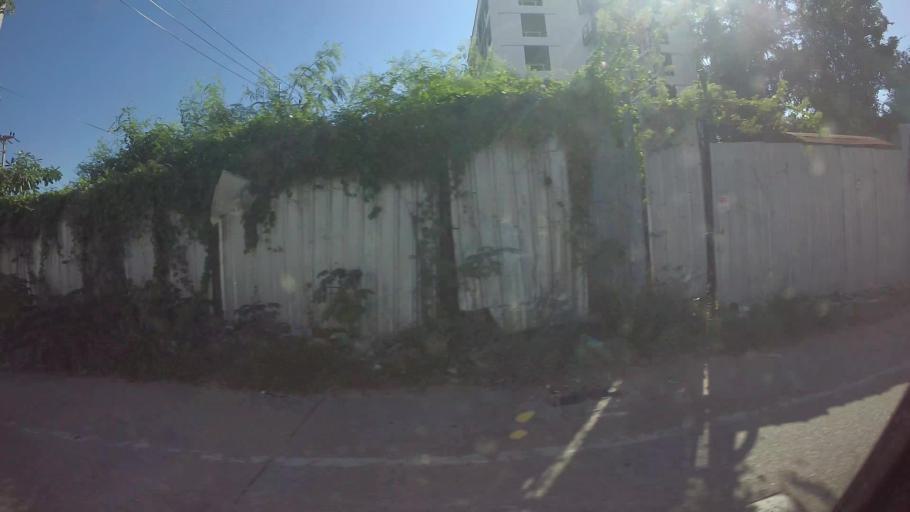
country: TH
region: Chon Buri
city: Phatthaya
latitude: 12.9103
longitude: 100.8806
